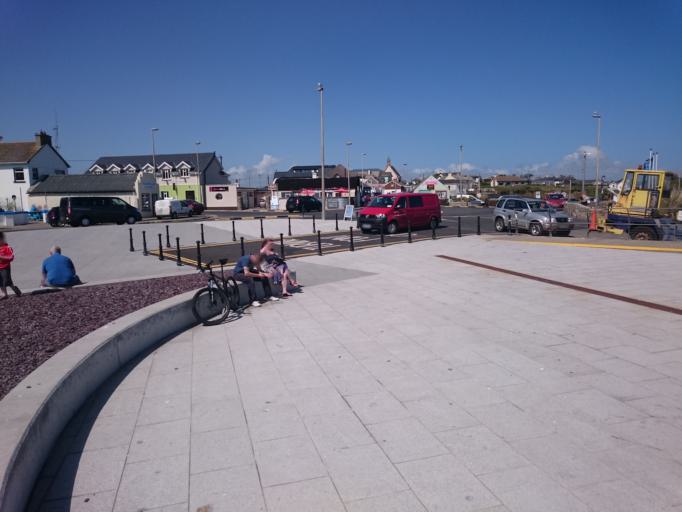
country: IE
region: Leinster
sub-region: Loch Garman
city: Loch Garman
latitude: 52.1724
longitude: -6.5893
